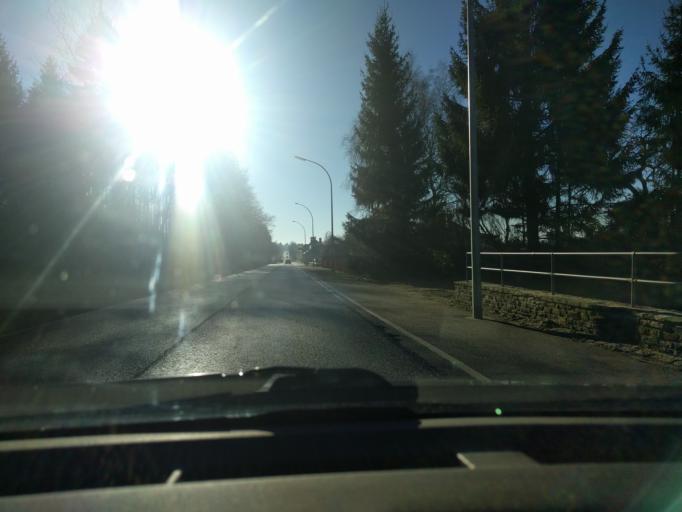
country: LU
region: Diekirch
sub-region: Canton de Clervaux
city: Troisvierges
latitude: 50.1734
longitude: 6.0253
